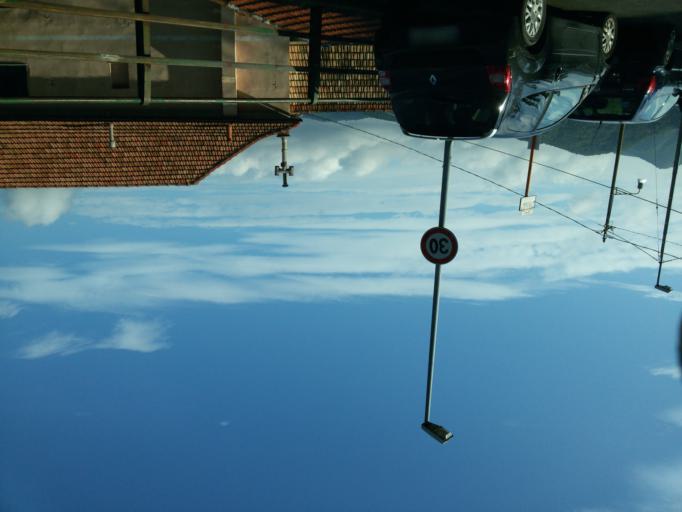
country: IT
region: Liguria
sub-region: Provincia di Genova
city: Piccarello
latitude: 44.4670
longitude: 8.9758
